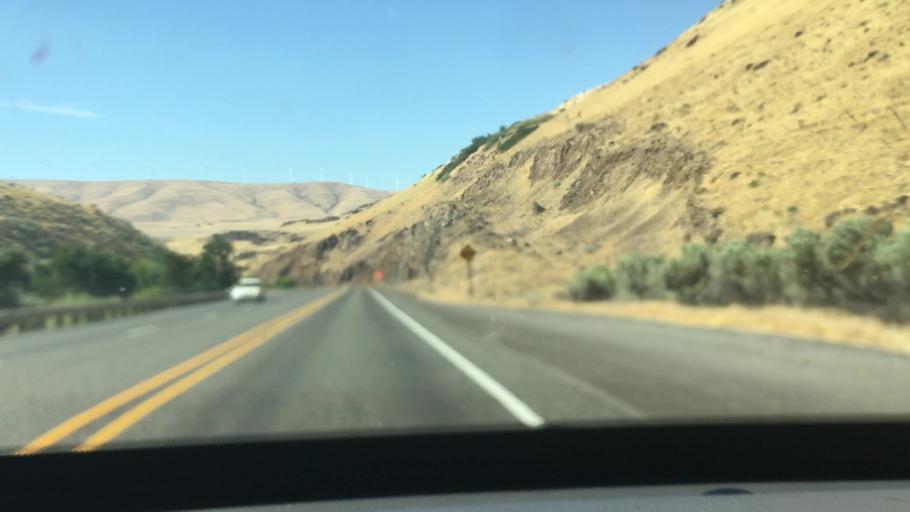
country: US
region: Washington
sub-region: Klickitat County
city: Goldendale
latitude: 45.6592
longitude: -120.8197
